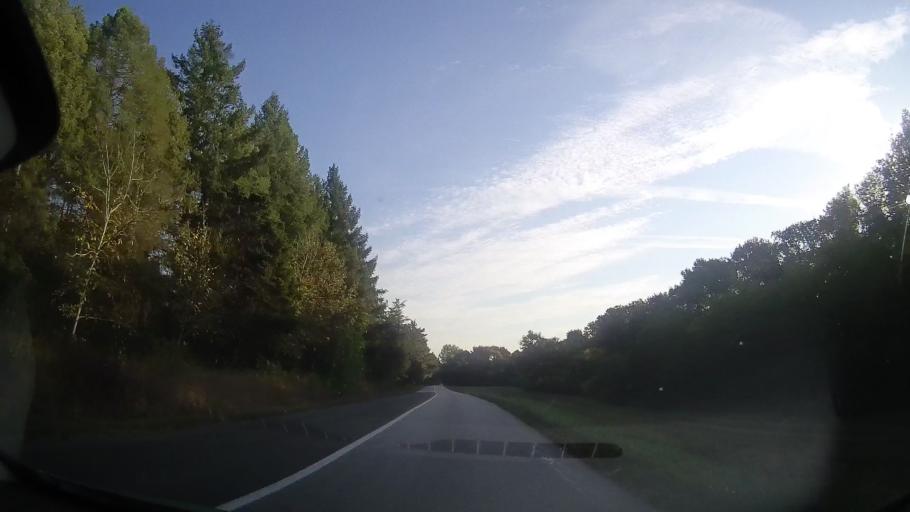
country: RO
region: Timis
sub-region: Comuna Pischia
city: Pischia
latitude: 45.9238
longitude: 21.3766
